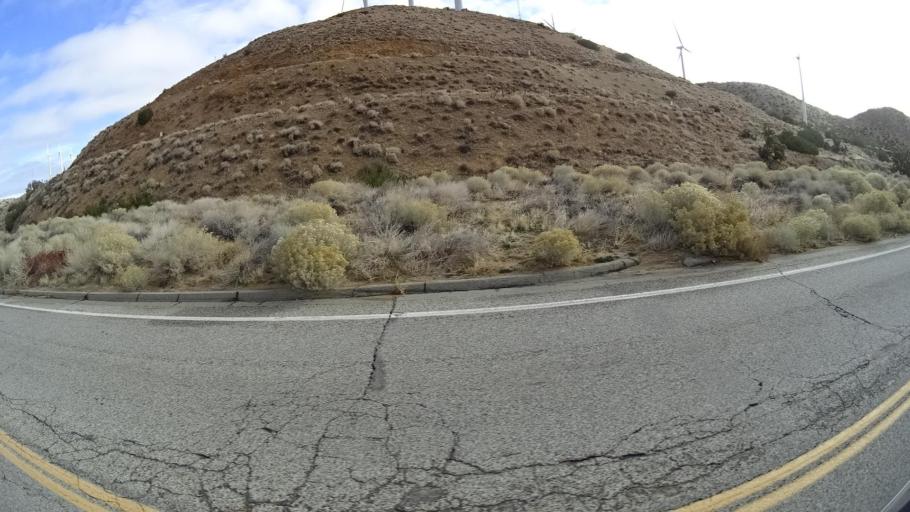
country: US
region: California
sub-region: Kern County
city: Tehachapi
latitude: 35.0285
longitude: -118.3527
